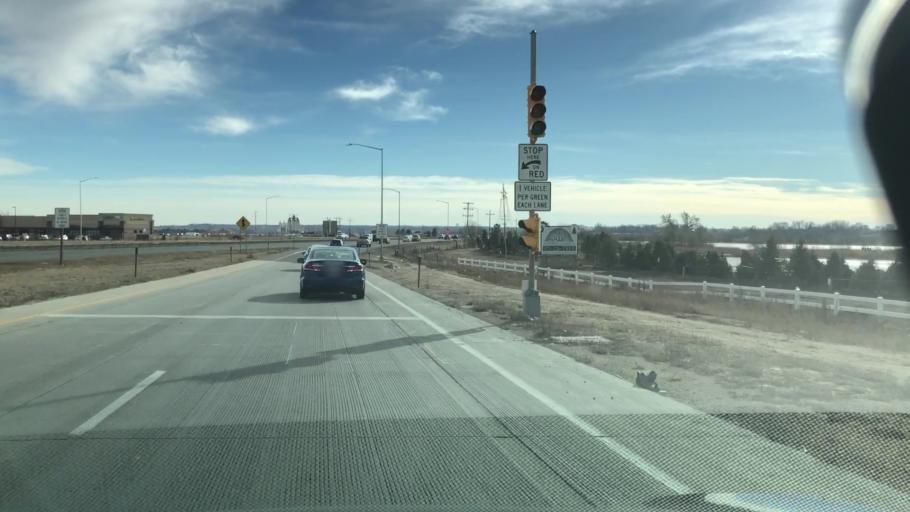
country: US
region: Colorado
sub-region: Weld County
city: Windsor
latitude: 40.5216
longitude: -104.9930
